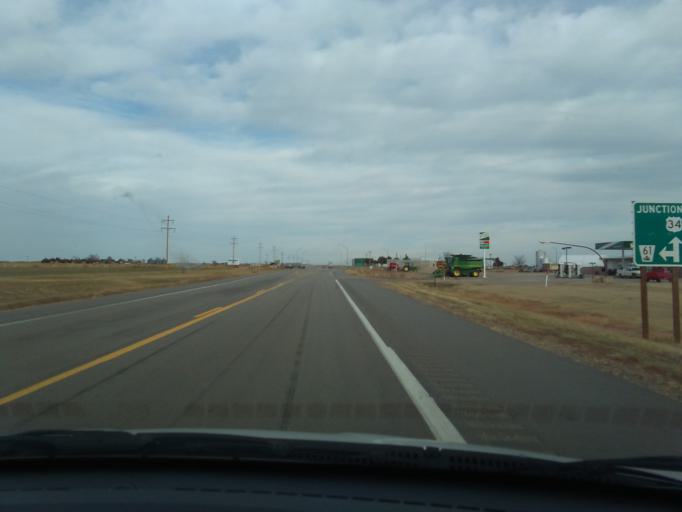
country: US
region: Nebraska
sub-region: Dundy County
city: Benkelman
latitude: 40.0594
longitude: -101.5351
